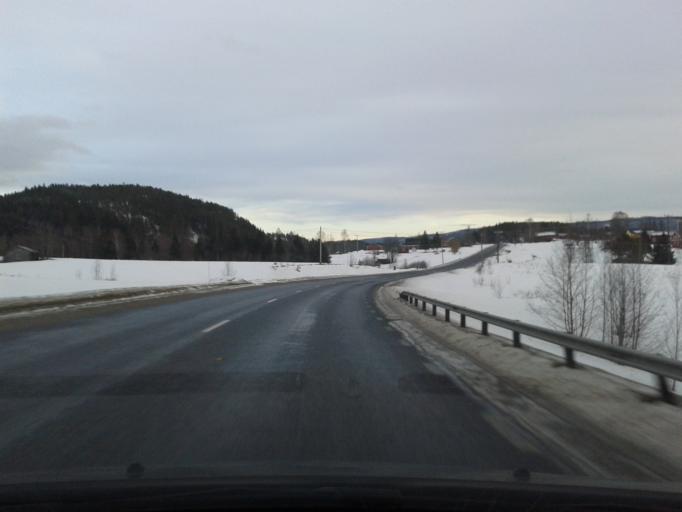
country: SE
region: Vaesternorrland
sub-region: Solleftea Kommun
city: Solleftea
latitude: 63.3494
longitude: 17.0621
